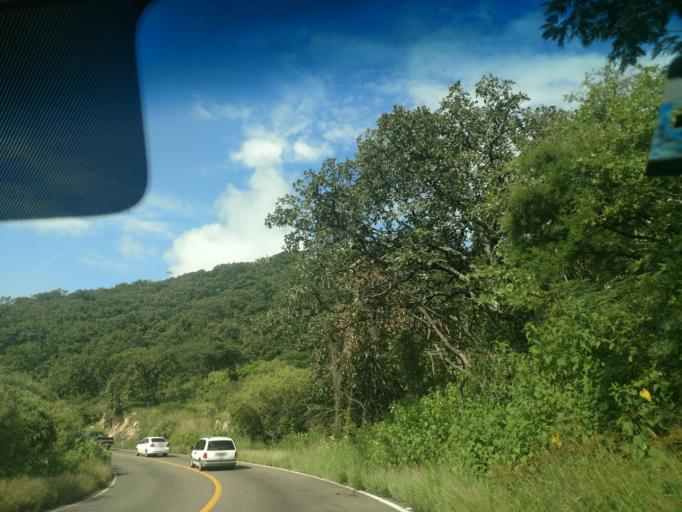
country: MX
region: Jalisco
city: El Salto
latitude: 20.4859
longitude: -104.3665
